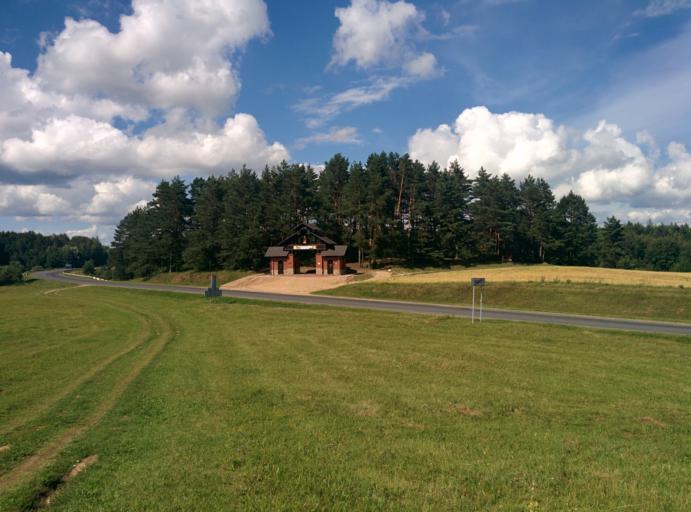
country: BY
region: Minsk
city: Myadzyel
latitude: 54.8952
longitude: 26.9062
